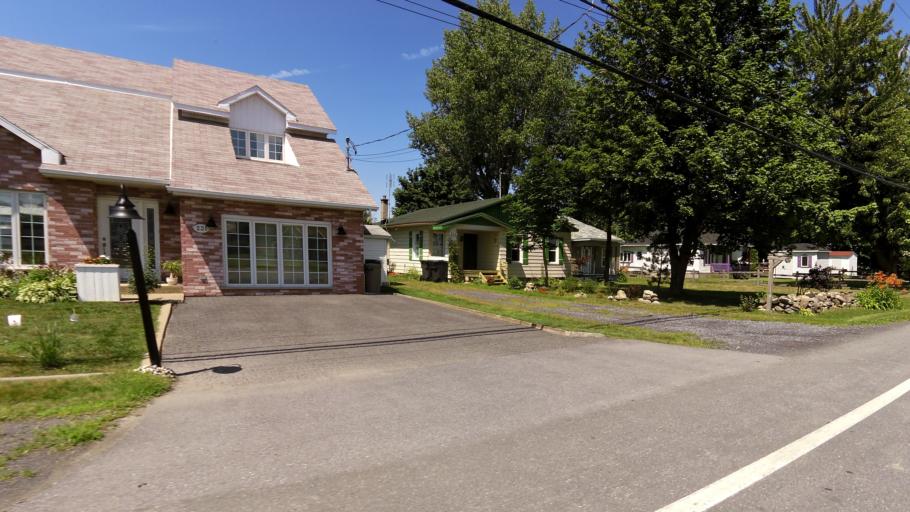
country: CA
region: Quebec
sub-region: Monteregie
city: Saint-Jean-sur-Richelieu
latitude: 45.3403
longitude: -73.2584
